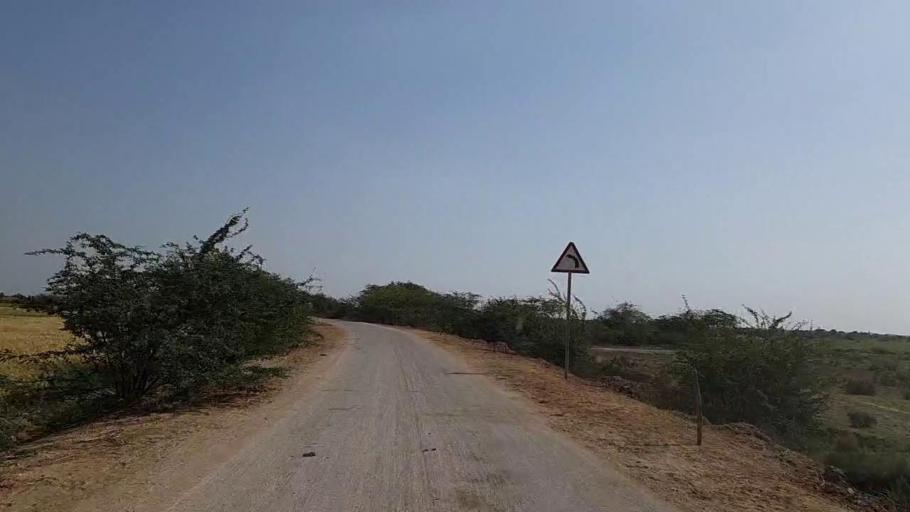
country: PK
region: Sindh
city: Daro Mehar
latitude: 24.7708
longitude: 68.1813
